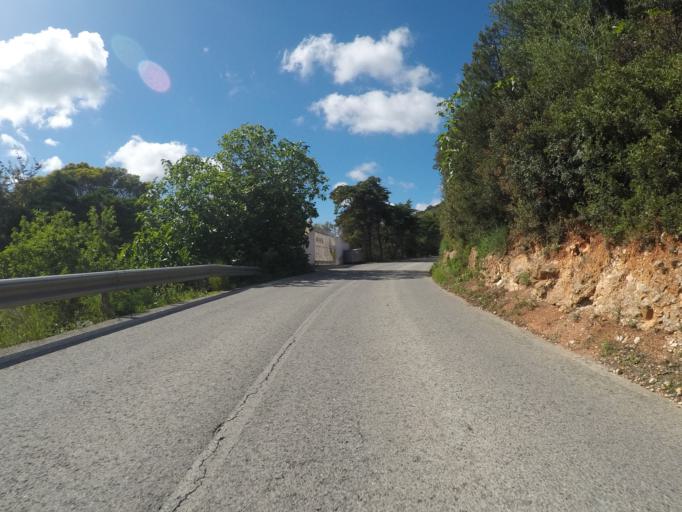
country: PT
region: Faro
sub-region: Vila do Bispo
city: Vila do Bispo
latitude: 37.0736
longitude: -8.8297
